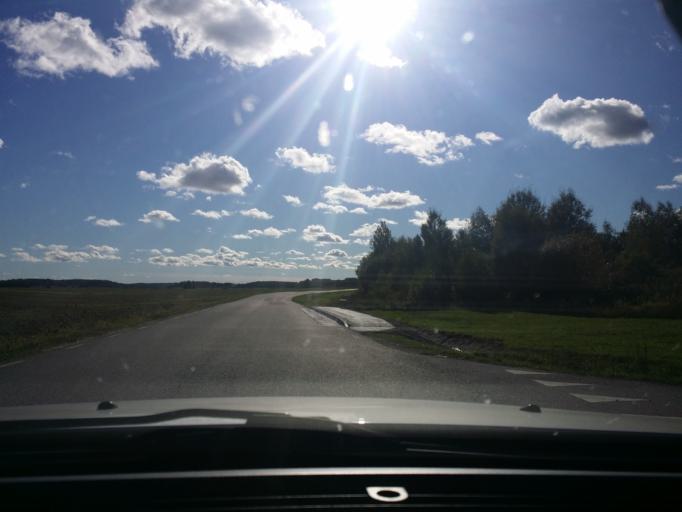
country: SE
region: Vaestmanland
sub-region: Vasteras
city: Vasteras
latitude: 59.5627
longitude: 16.4773
